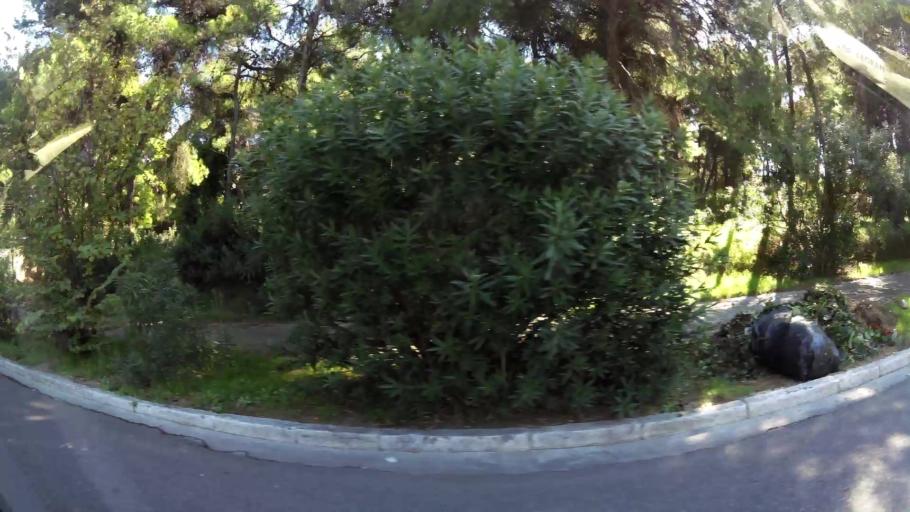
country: GR
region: Attica
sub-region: Nomarchia Athinas
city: Ekali
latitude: 38.1097
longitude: 23.8407
